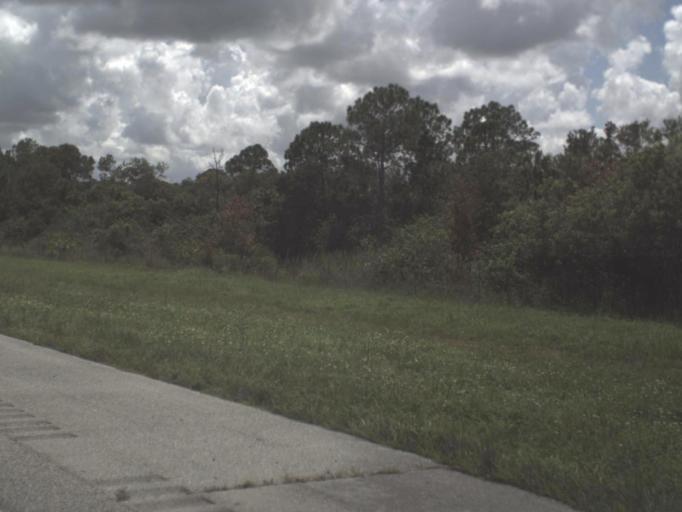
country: US
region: Florida
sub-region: Collier County
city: Orangetree
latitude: 26.1529
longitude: -81.5279
